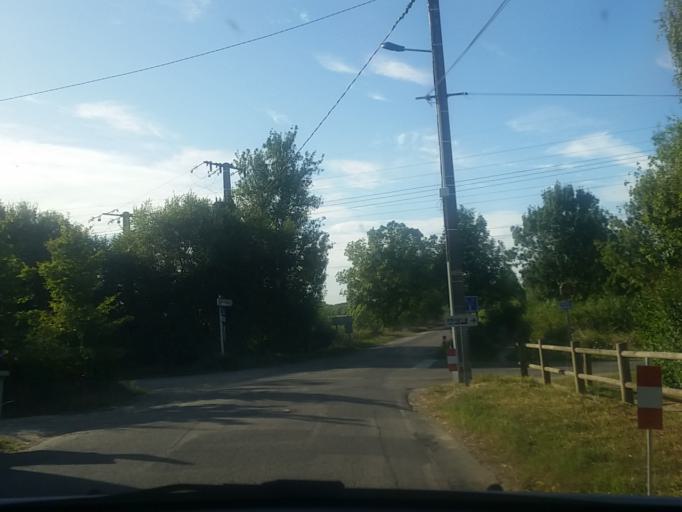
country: FR
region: Pays de la Loire
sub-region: Departement de la Loire-Atlantique
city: Bouguenais
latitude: 47.1810
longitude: -1.6327
